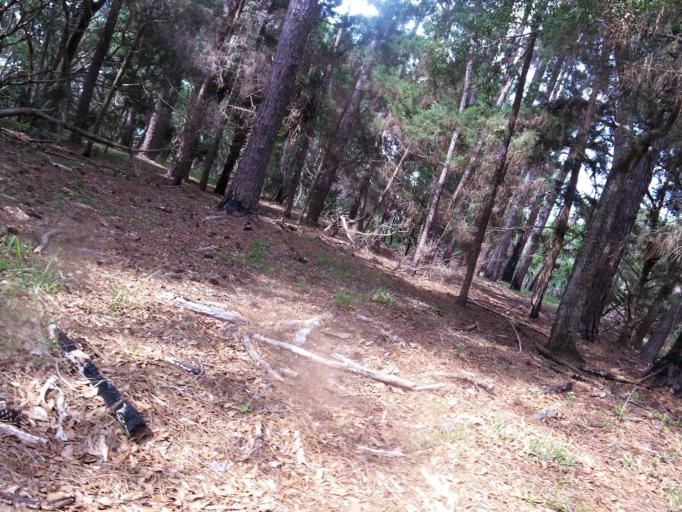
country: US
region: Florida
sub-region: Saint Johns County
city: Villano Beach
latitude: 30.0149
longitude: -81.3453
